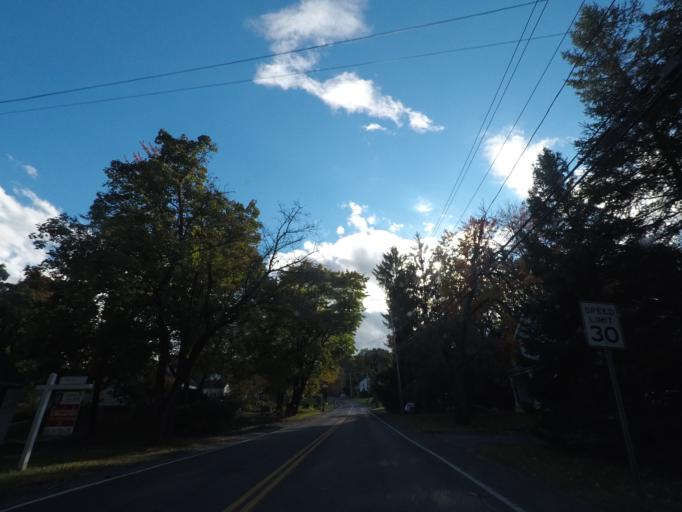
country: US
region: New York
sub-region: Schenectady County
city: Niskayuna
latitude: 42.7700
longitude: -73.8264
